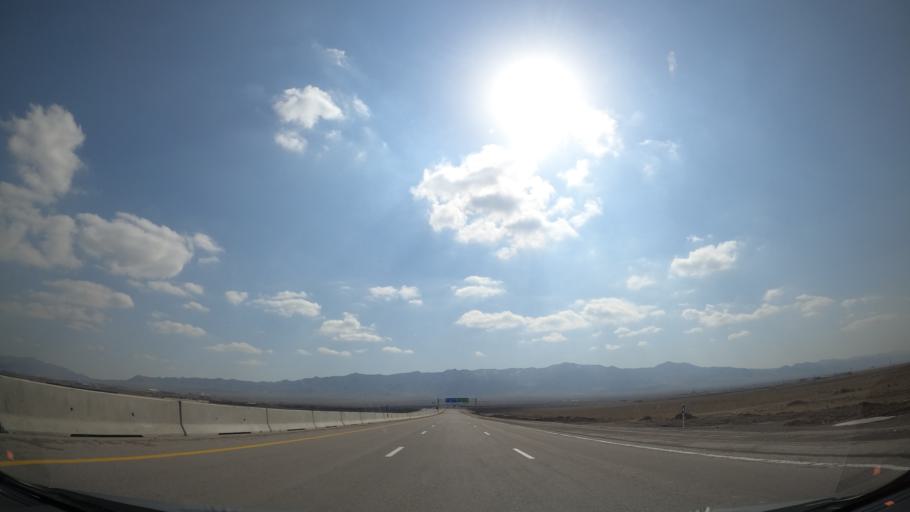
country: IR
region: Alborz
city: Eshtehard
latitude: 35.7412
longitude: 50.5608
